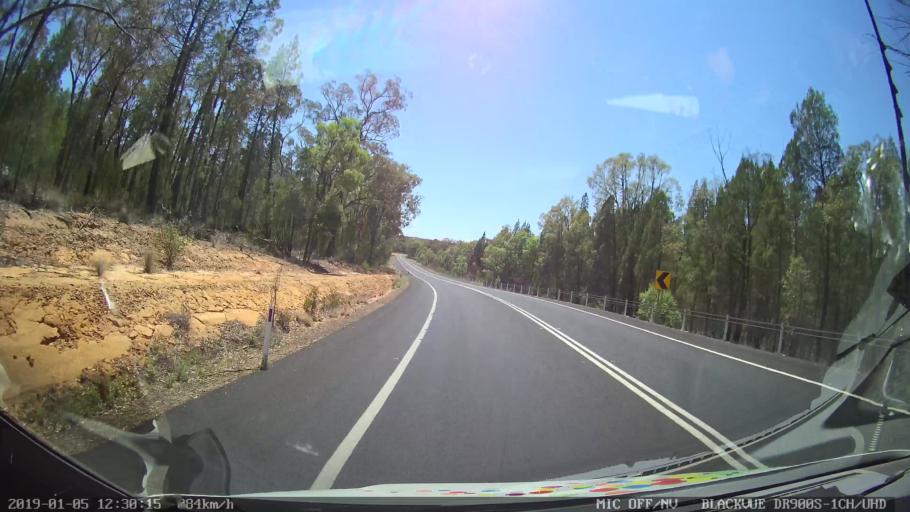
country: AU
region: New South Wales
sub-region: Warrumbungle Shire
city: Coonabarabran
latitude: -31.2293
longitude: 149.3481
